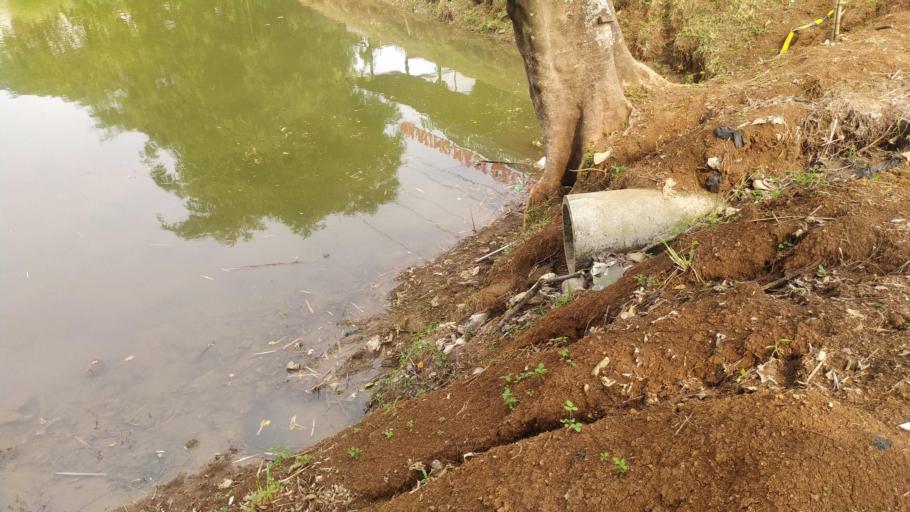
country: ID
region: West Java
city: Pamulang
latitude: -6.3227
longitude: 106.7852
